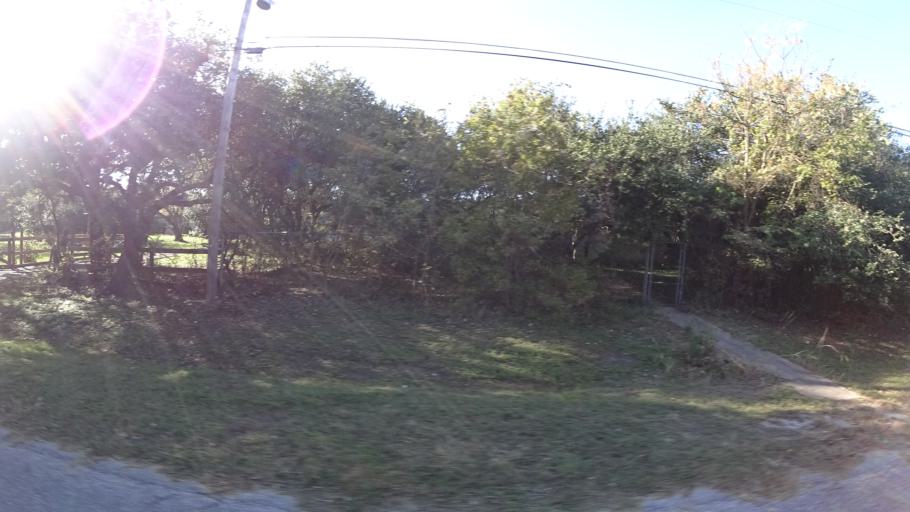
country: US
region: Texas
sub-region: Travis County
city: Barton Creek
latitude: 30.2429
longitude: -97.9153
